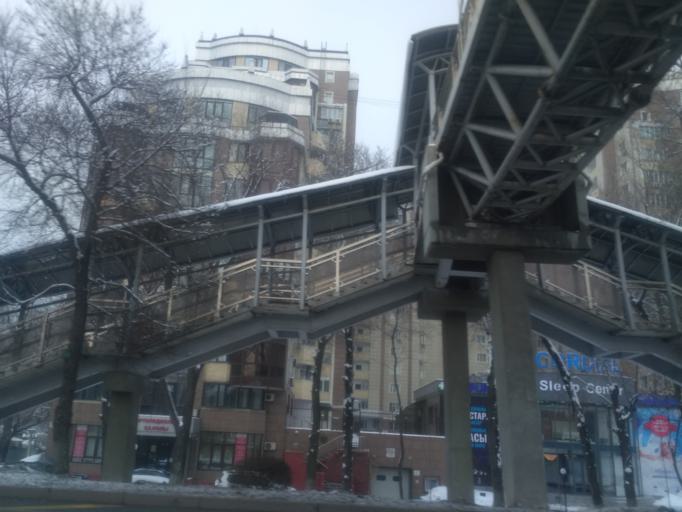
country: KZ
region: Almaty Qalasy
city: Almaty
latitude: 43.2229
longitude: 76.9362
